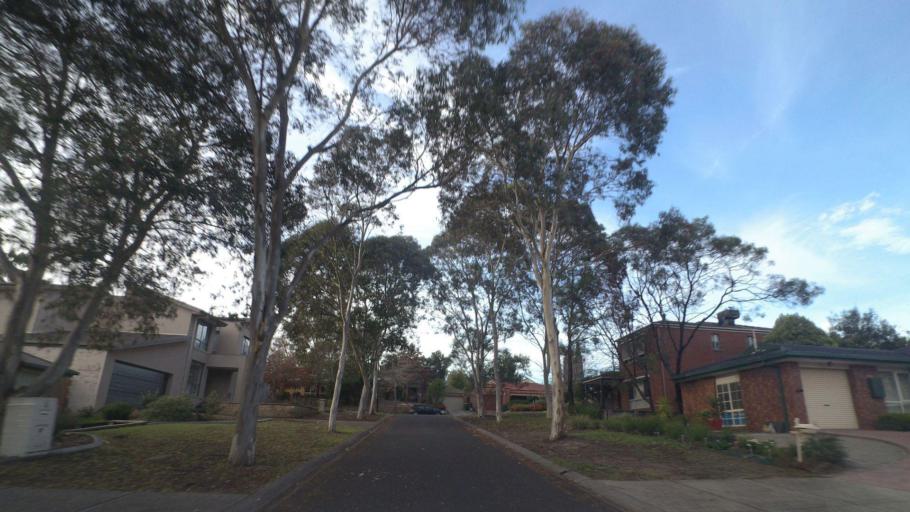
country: AU
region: Victoria
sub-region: Banyule
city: Yallambie
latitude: -37.7248
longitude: 145.1005
